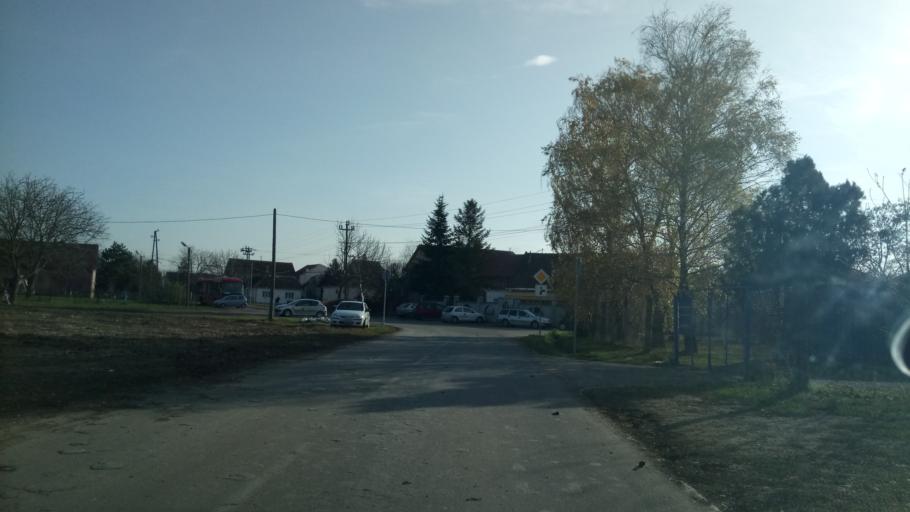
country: RS
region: Autonomna Pokrajina Vojvodina
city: Nova Pazova
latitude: 44.9536
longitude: 20.2256
